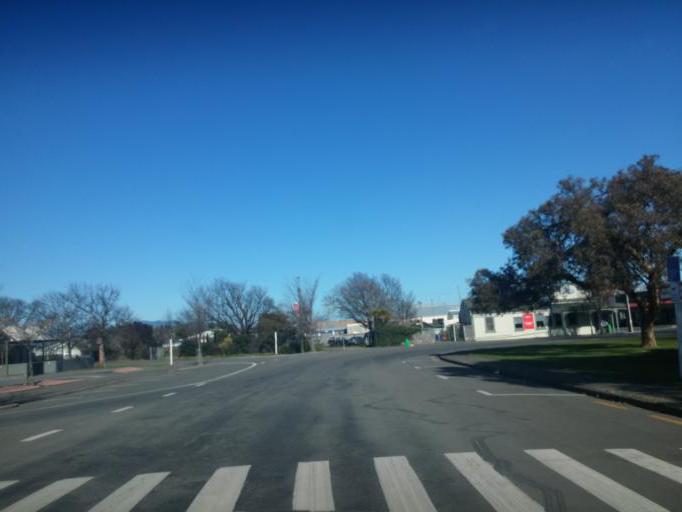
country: NZ
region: Wellington
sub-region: South Wairarapa District
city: Waipawa
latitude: -41.2188
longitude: 175.4600
